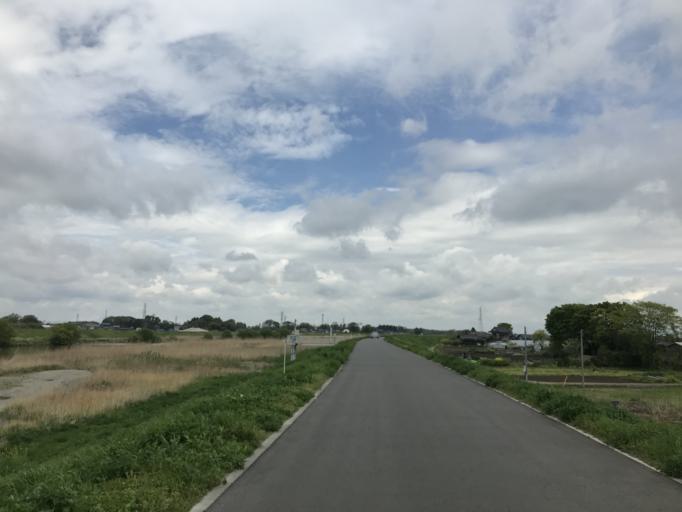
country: JP
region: Ibaraki
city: Mitsukaido
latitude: 35.9975
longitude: 139.9930
